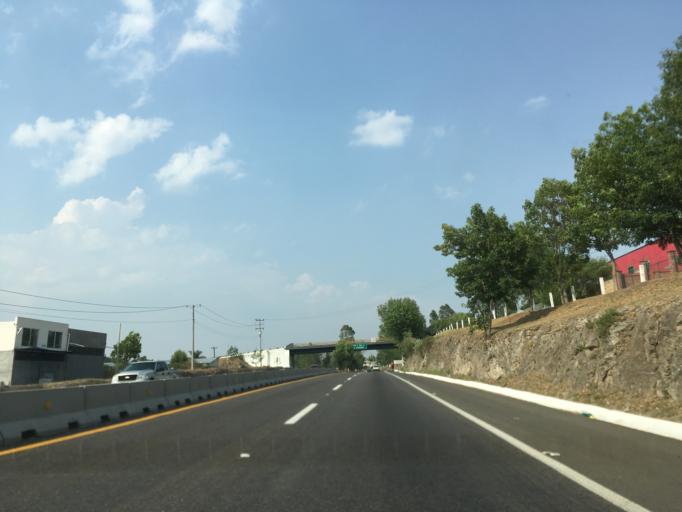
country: MX
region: Michoacan
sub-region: Morelia
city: Morelos
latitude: 19.6426
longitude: -101.2531
